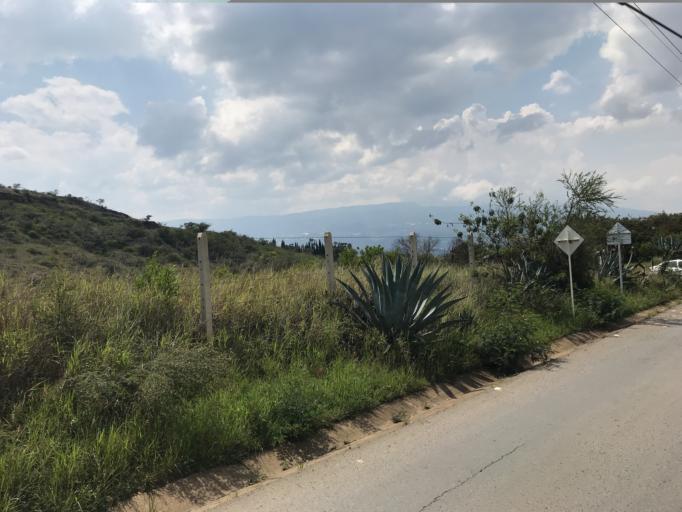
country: CO
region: Boyaca
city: Sachica
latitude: 5.6098
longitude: -73.5356
